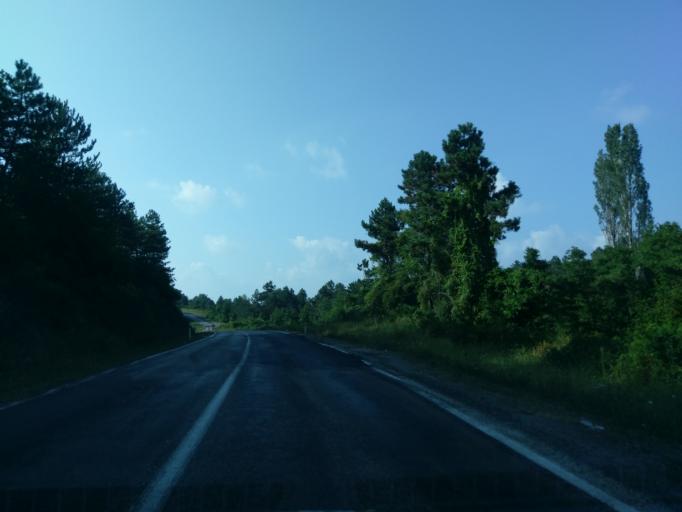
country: TR
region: Sinop
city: Yenikonak
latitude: 41.9405
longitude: 34.7064
